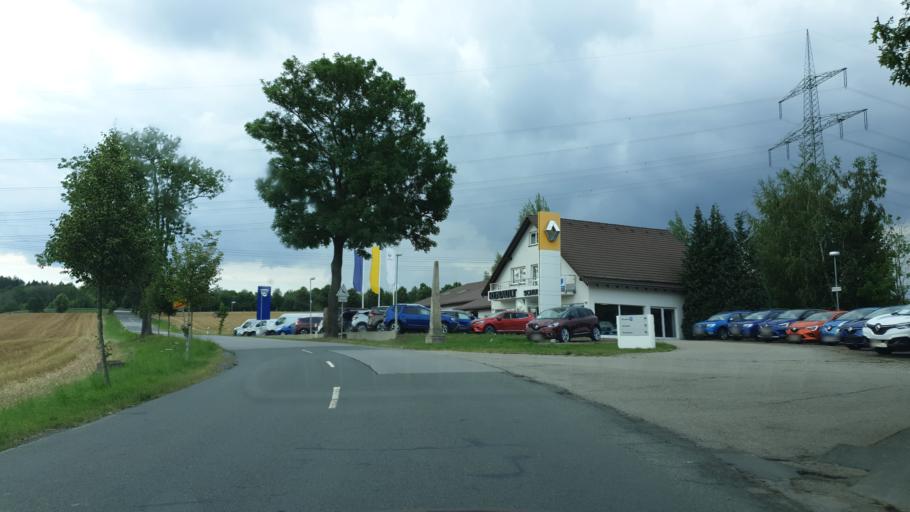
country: DE
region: Saxony
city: Zwonitz
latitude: 50.6494
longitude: 12.8187
